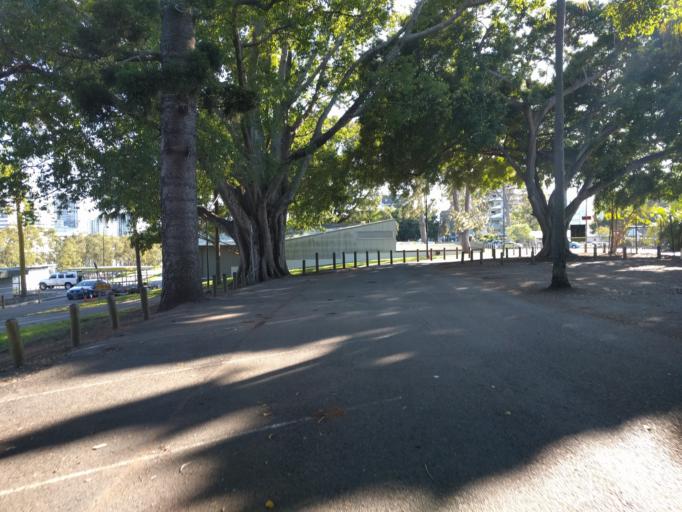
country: AU
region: Queensland
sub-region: Brisbane
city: Milton
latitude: -27.4785
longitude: 153.0038
